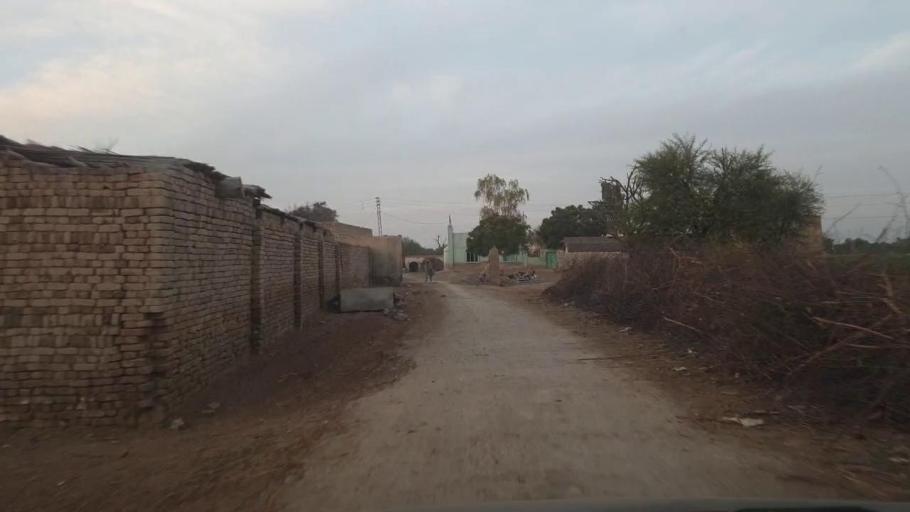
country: PK
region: Sindh
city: Shahpur Chakar
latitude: 26.0684
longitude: 68.5362
